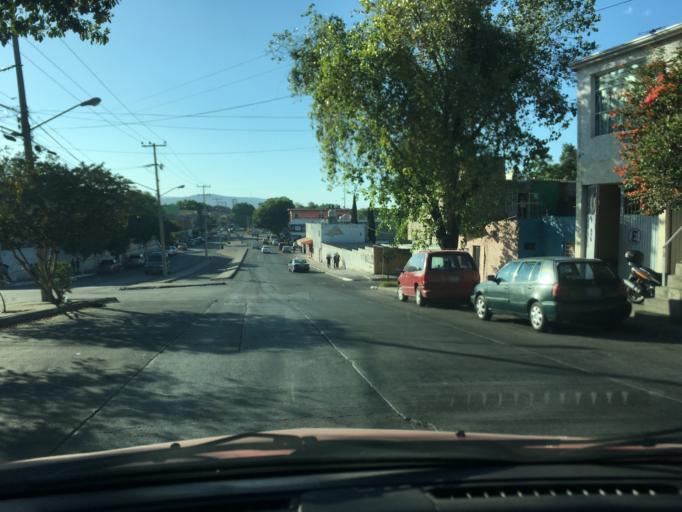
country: MX
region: Jalisco
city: Guadalajara
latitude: 20.6196
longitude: -103.3876
